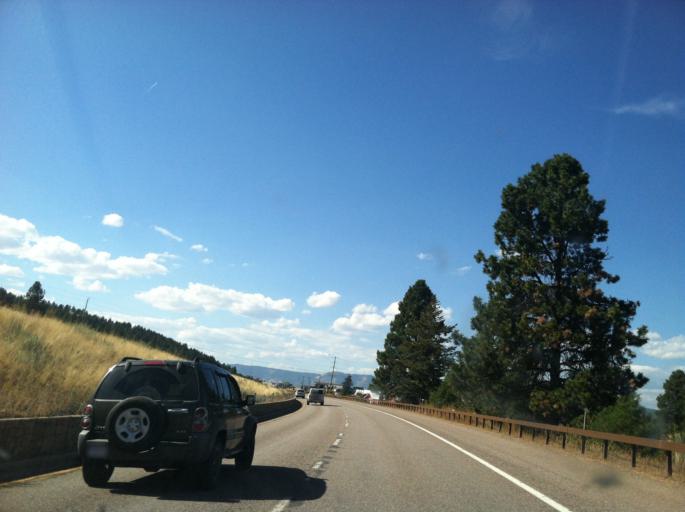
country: US
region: Montana
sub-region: Lake County
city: Polson
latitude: 47.6779
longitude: -114.1101
